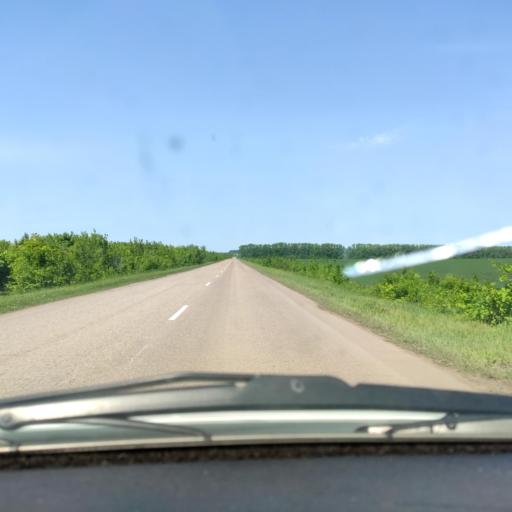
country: RU
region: Bashkortostan
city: Avdon
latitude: 54.5296
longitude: 55.6400
